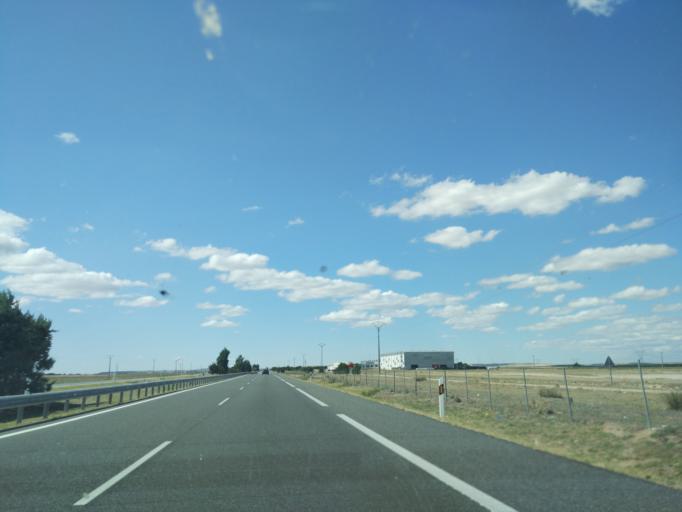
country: ES
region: Castille and Leon
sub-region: Provincia de Valladolid
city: San Vicente del Palacio
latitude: 41.2515
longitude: -4.8711
